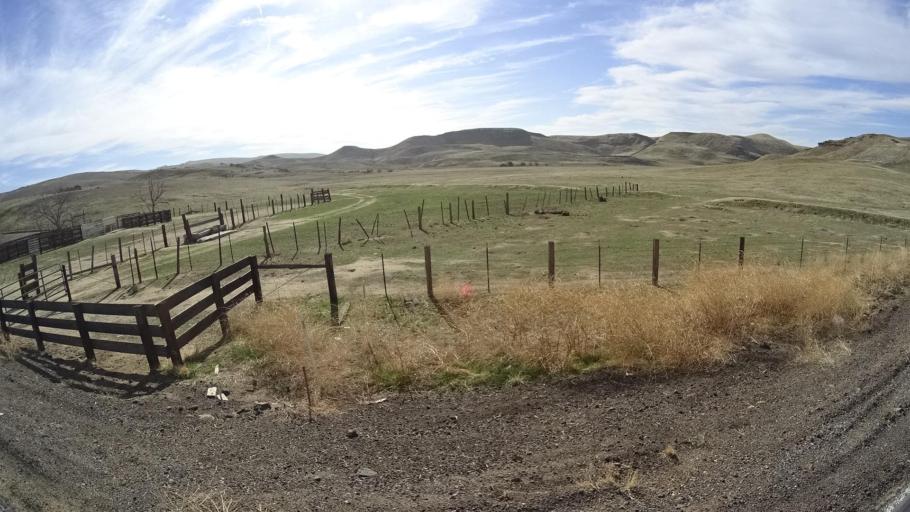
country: US
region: California
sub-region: Kern County
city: Oildale
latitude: 35.6131
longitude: -118.8726
